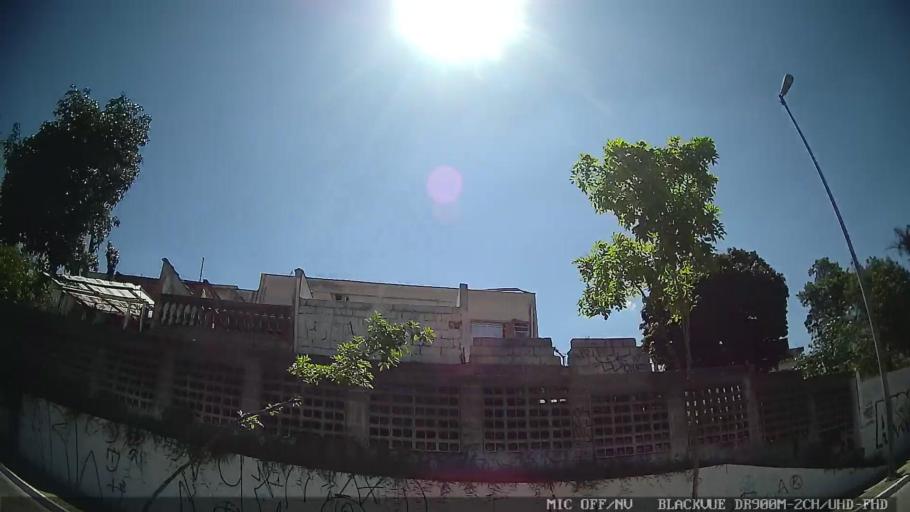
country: BR
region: Sao Paulo
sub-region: Sao Caetano Do Sul
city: Sao Caetano do Sul
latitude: -23.5728
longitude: -46.5199
